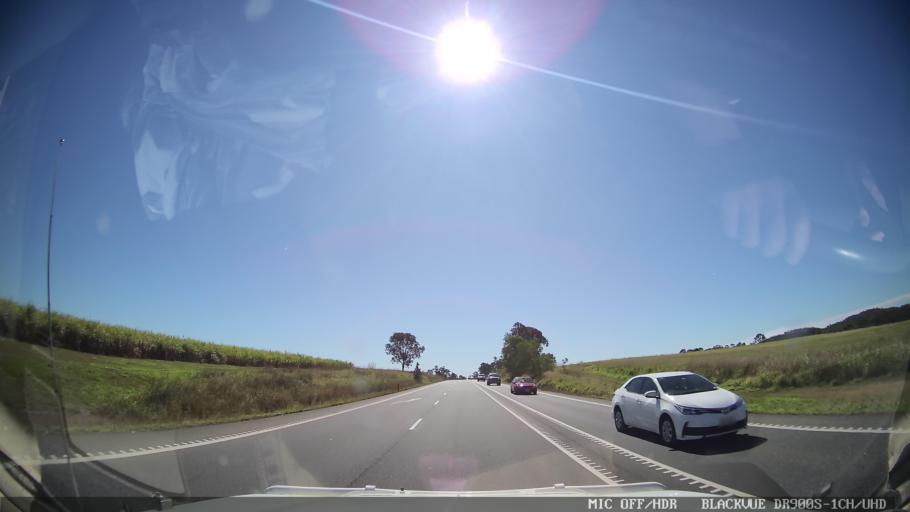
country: AU
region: Queensland
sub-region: Fraser Coast
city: Maryborough
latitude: -25.7840
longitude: 152.5966
